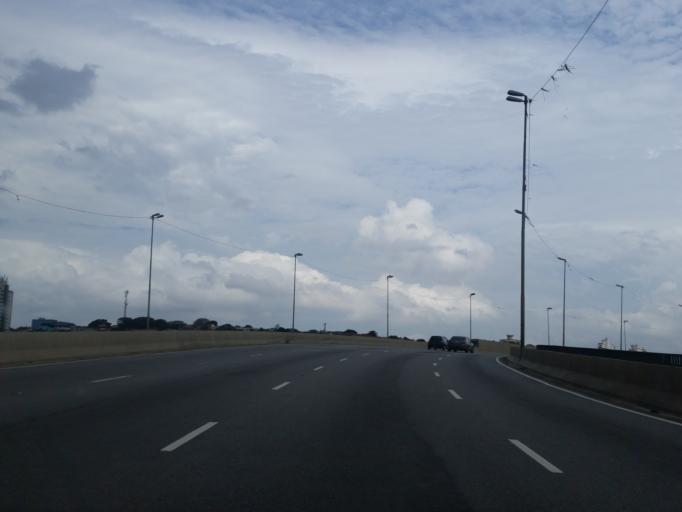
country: BR
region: Sao Paulo
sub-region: Guarulhos
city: Guarulhos
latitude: -23.4906
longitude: -46.4531
